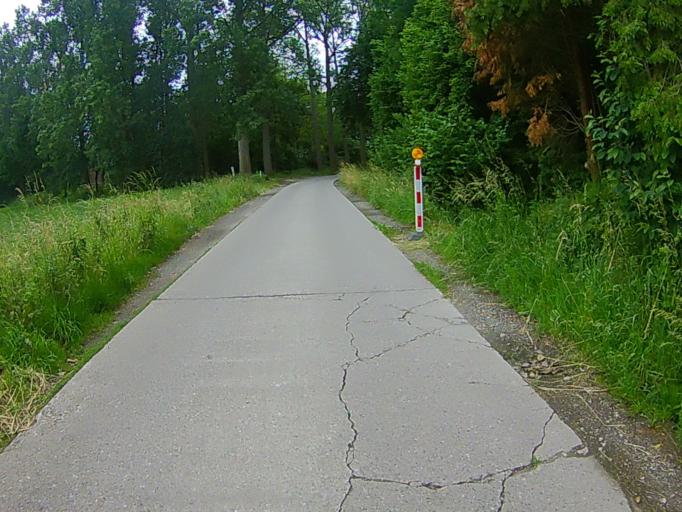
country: BE
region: Flanders
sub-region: Provincie Antwerpen
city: Ranst
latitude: 51.1627
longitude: 4.5579
